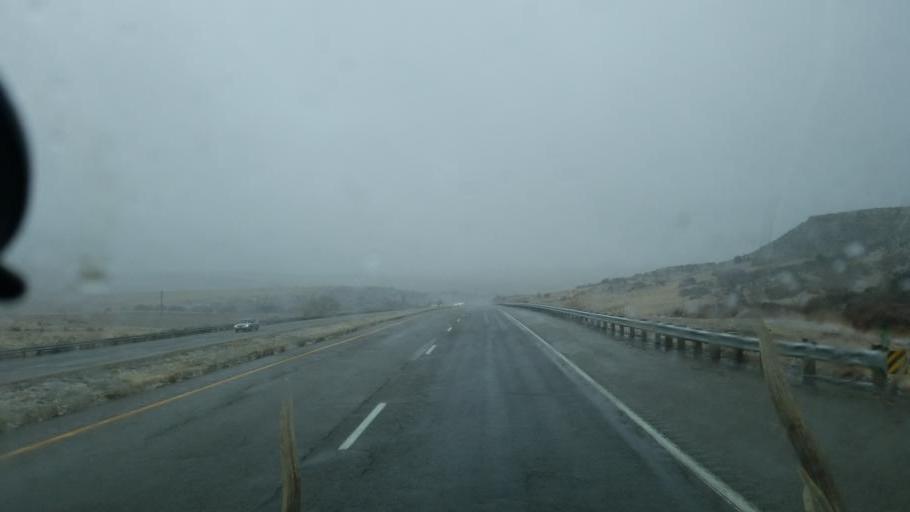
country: US
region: Colorado
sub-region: Pueblo County
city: Colorado City
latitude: 37.9001
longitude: -104.8288
